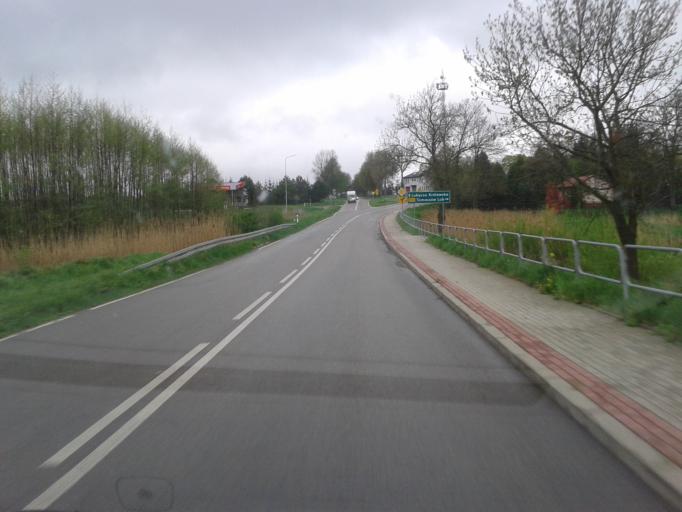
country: PL
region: Lublin Voivodeship
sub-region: Powiat tomaszowski
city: Telatyn
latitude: 50.5251
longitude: 23.9144
